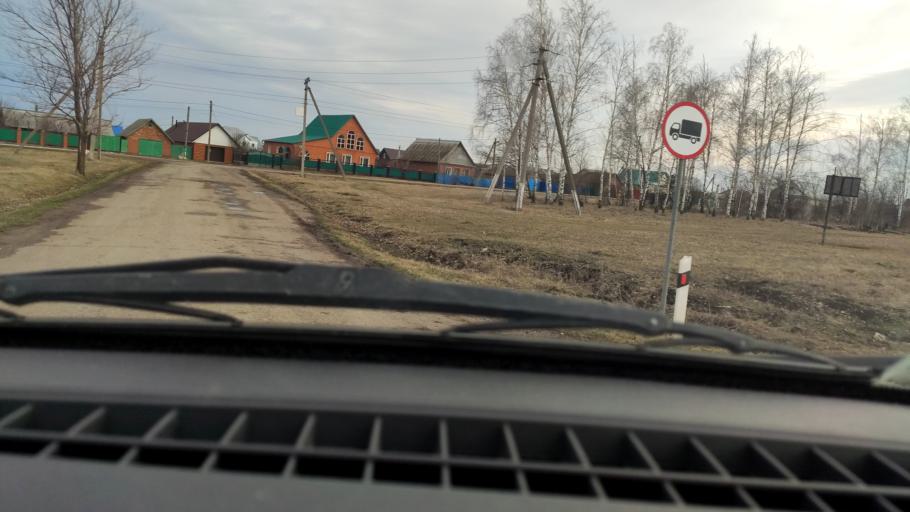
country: RU
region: Bashkortostan
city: Davlekanovo
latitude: 54.2349
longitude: 55.0287
